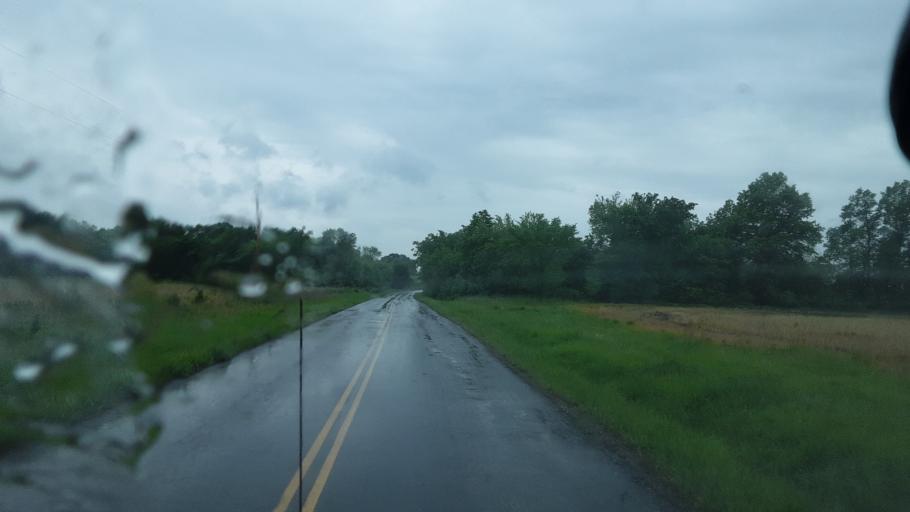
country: US
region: Missouri
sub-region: Randolph County
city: Moberly
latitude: 39.3882
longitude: -92.2486
